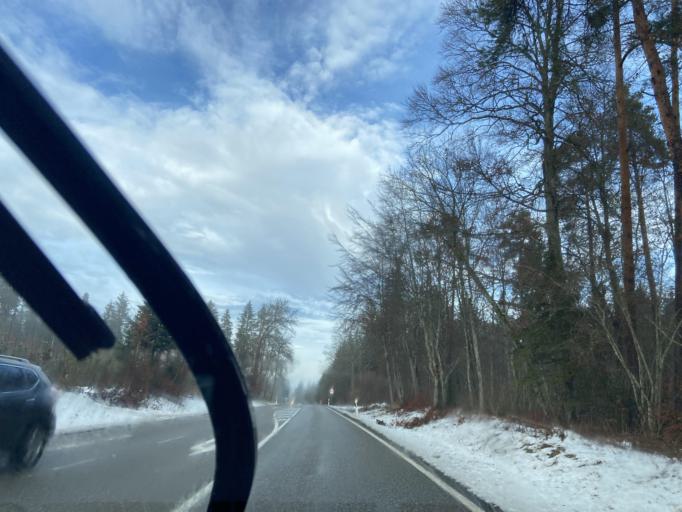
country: DE
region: Baden-Wuerttemberg
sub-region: Tuebingen Region
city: Hettingen
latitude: 48.2264
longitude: 9.2883
